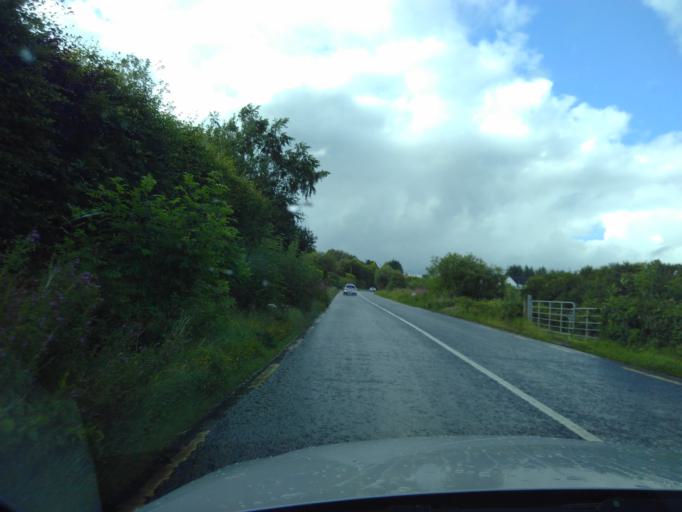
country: IE
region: Ulster
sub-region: County Donegal
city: Letterkenny
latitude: 54.9694
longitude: -7.6894
